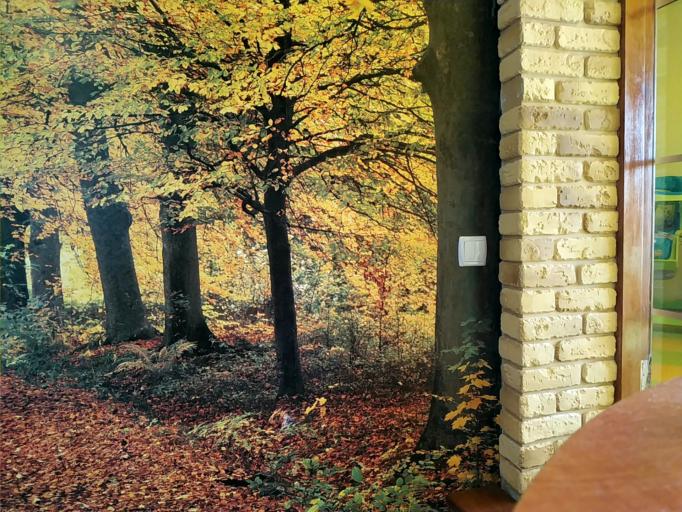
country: RU
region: Novgorod
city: Staraya Russa
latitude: 57.8377
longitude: 31.4645
